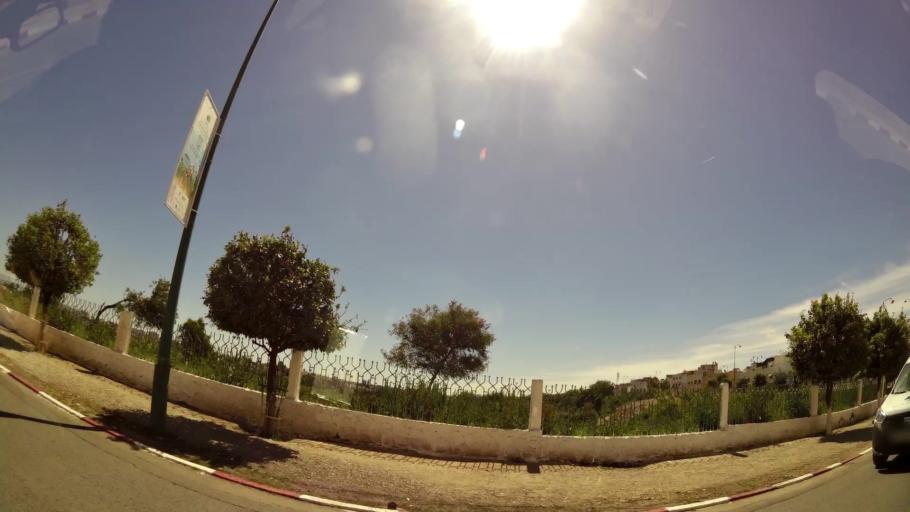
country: MA
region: Meknes-Tafilalet
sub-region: Meknes
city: Meknes
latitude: 33.8859
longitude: -5.5531
